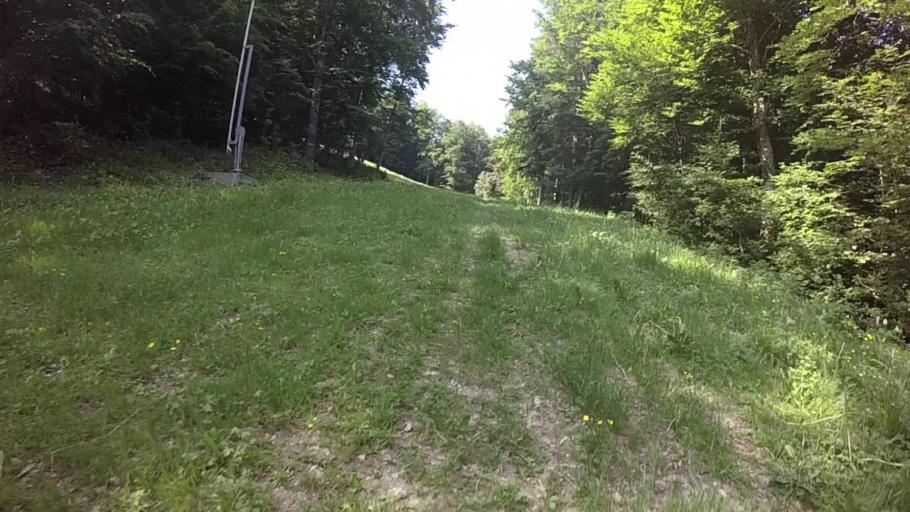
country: FR
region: Provence-Alpes-Cote d'Azur
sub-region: Departement des Alpes-de-Haute-Provence
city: Seyne-les-Alpes
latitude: 44.4073
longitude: 6.3521
